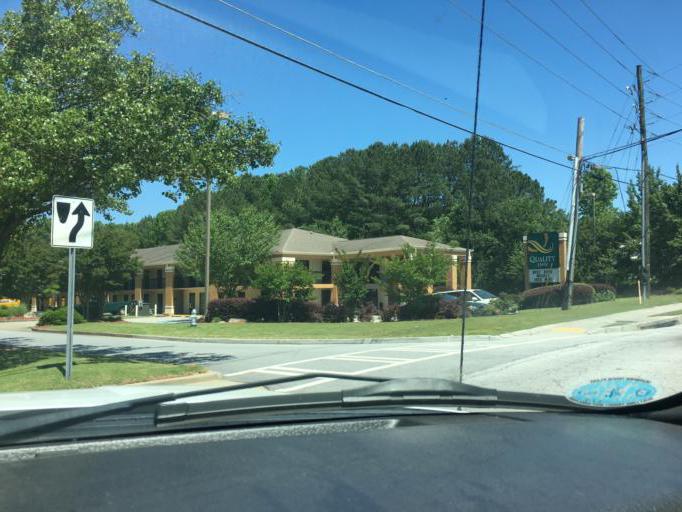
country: US
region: Georgia
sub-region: Gwinnett County
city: Mountain Park
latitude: 33.8264
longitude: -84.1137
